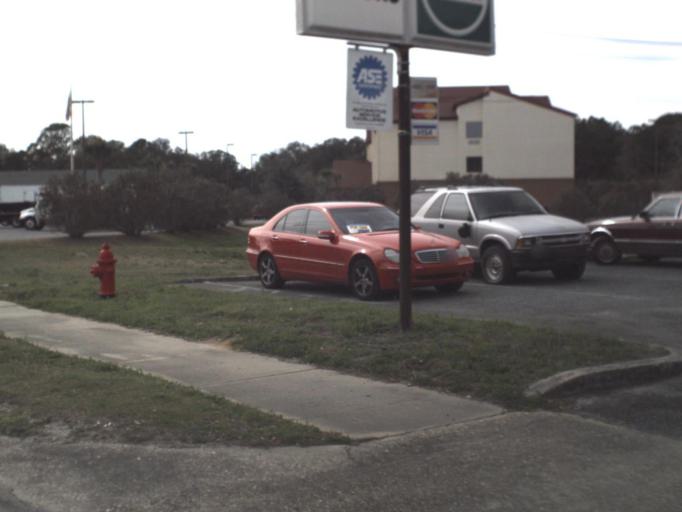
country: US
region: Florida
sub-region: Bay County
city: Panama City
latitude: 30.1783
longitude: -85.6568
